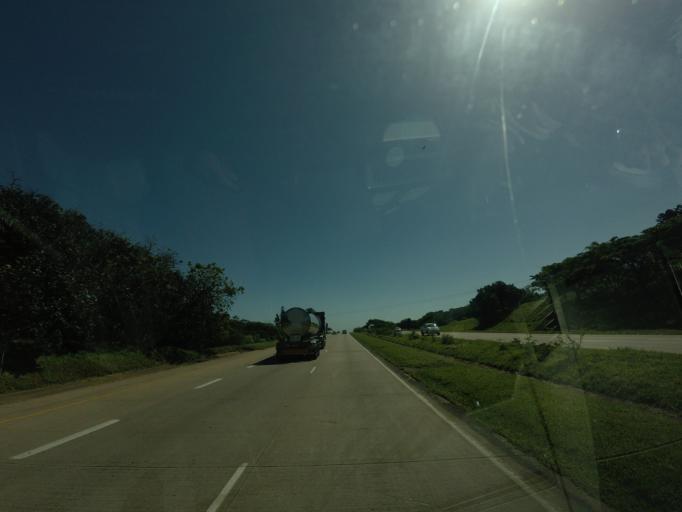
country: ZA
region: KwaZulu-Natal
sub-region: iLembe District Municipality
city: Ballitoville
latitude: -29.4950
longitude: 31.2152
